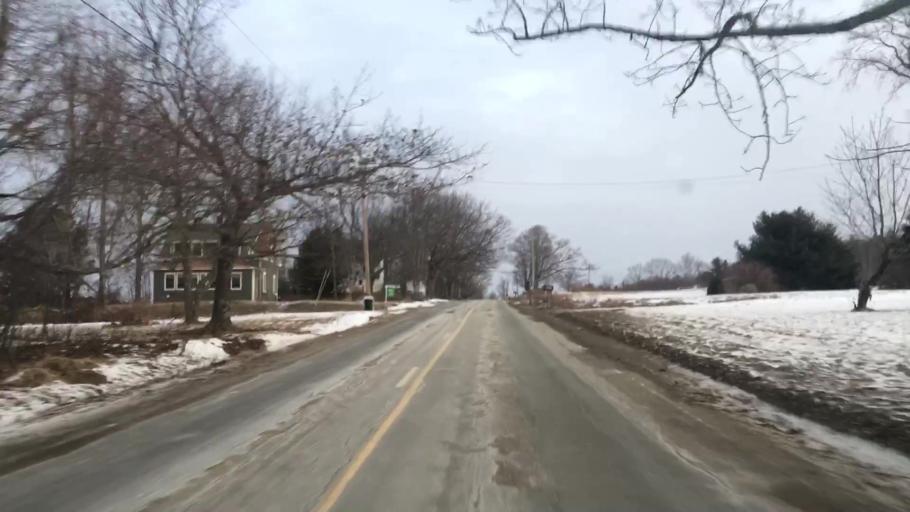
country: US
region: Maine
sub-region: Hancock County
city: Franklin
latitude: 44.7068
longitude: -68.3402
